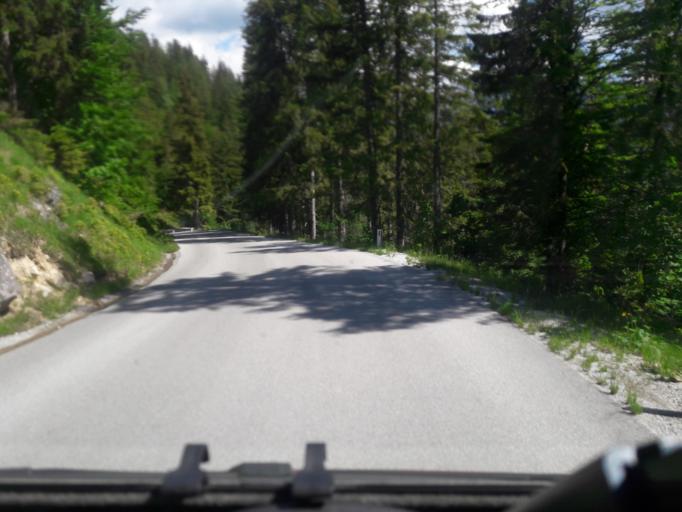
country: AT
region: Styria
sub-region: Politischer Bezirk Liezen
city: Tauplitz
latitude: 47.5822
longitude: 13.9633
